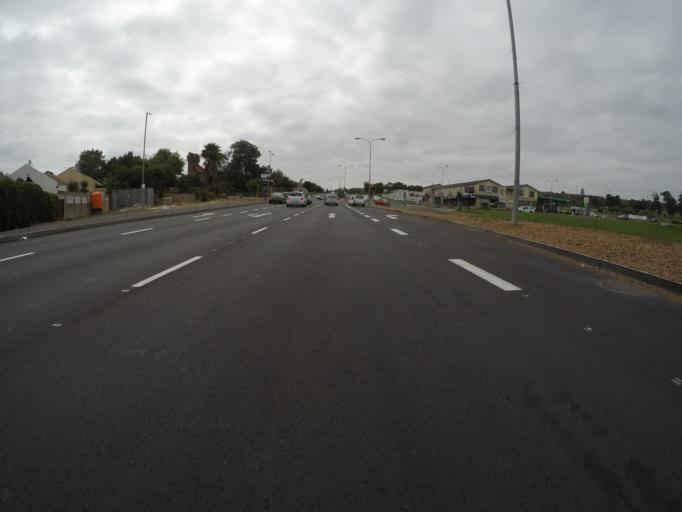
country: ZA
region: Western Cape
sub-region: City of Cape Town
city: Kraaifontein
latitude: -33.8635
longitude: 18.6328
